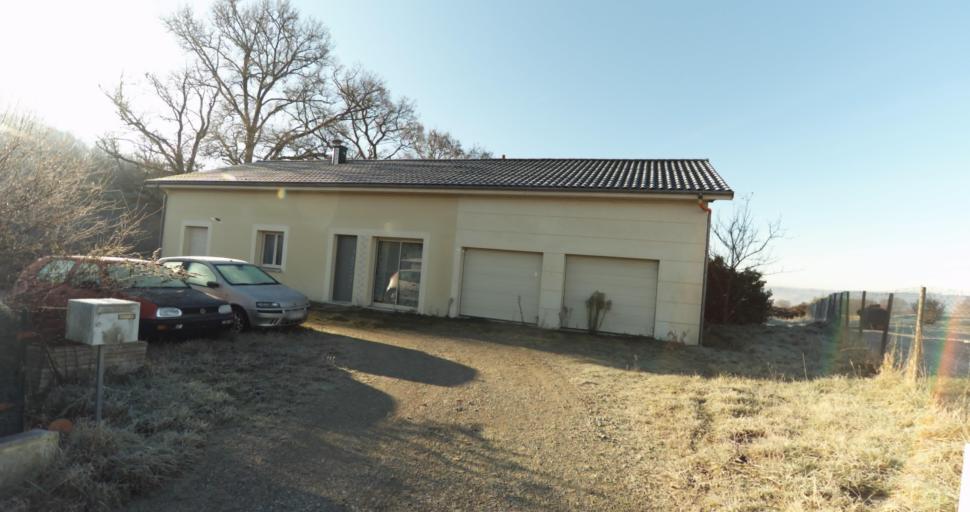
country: FR
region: Limousin
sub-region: Departement de la Haute-Vienne
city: Aixe-sur-Vienne
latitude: 45.8084
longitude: 1.1386
